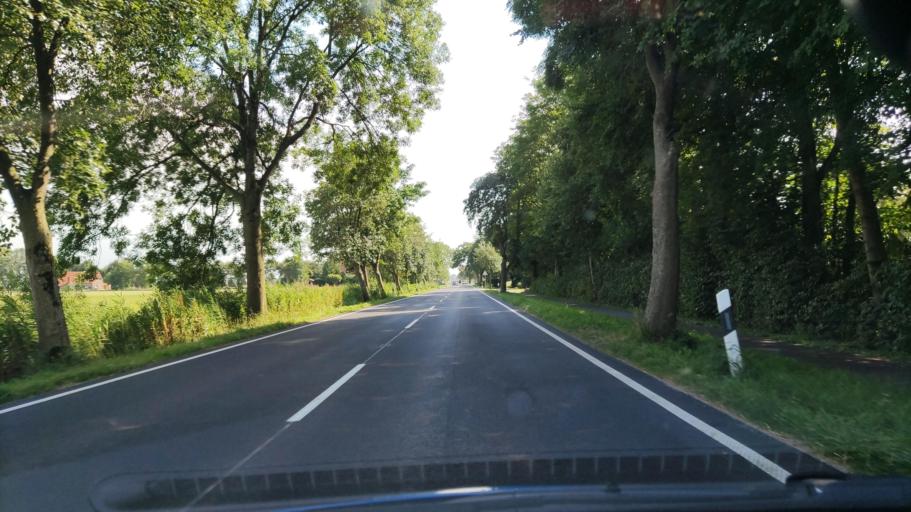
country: DE
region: Lower Saxony
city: Werdum
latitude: 53.6595
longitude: 7.7897
